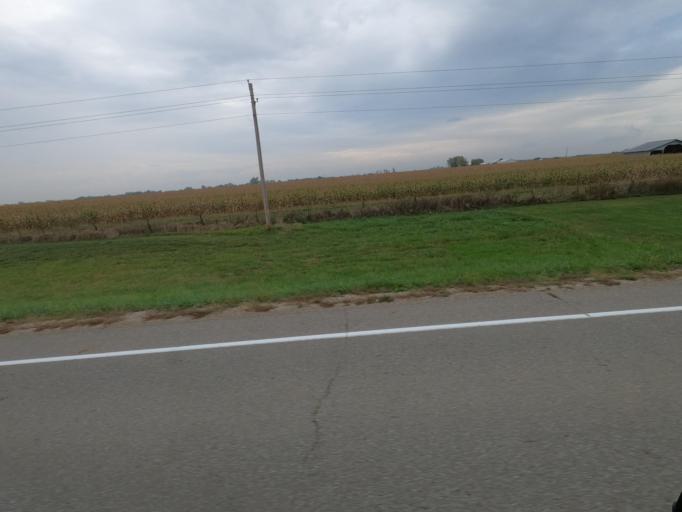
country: US
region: Iowa
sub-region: Henry County
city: Mount Pleasant
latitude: 40.8135
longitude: -91.7397
